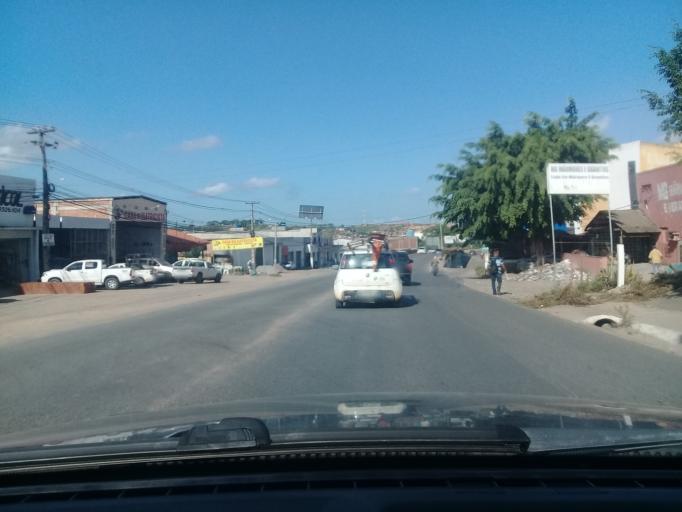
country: BR
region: Pernambuco
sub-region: Vitoria De Santo Antao
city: Vitoria de Santo Antao
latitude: -8.1122
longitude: -35.2912
